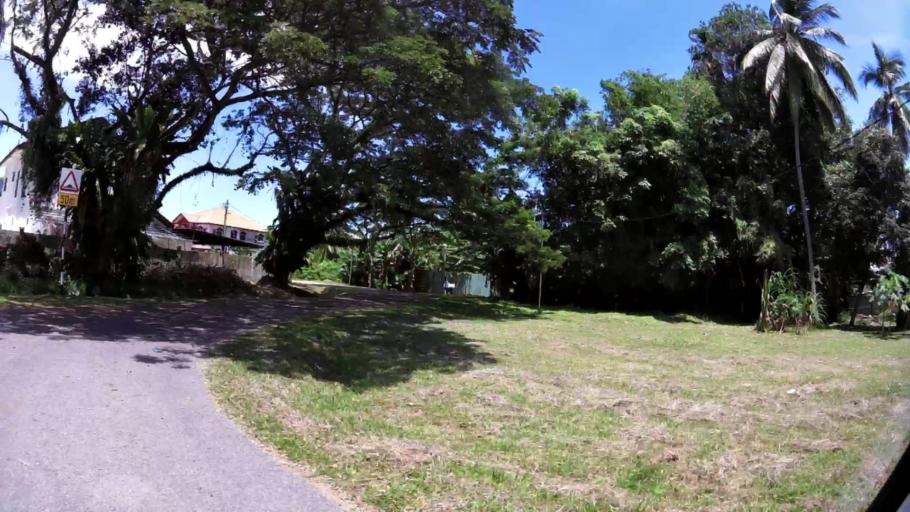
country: BN
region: Brunei and Muara
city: Bandar Seri Begawan
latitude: 4.9356
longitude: 114.9459
